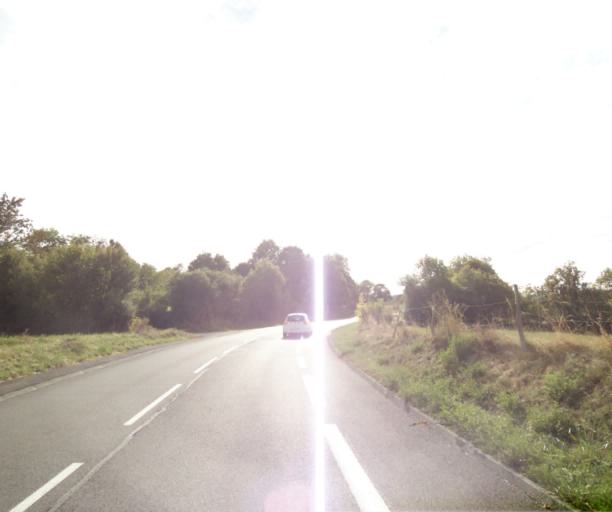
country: FR
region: Auvergne
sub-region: Departement du Puy-de-Dome
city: Romagnat
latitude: 45.7195
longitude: 3.0931
